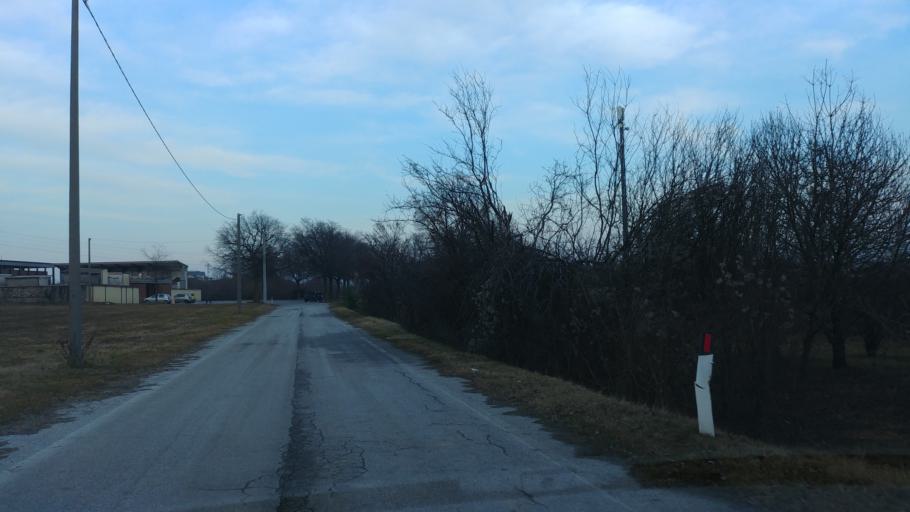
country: IT
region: Piedmont
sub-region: Provincia di Cuneo
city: Cuneo
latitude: 44.3962
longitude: 7.5278
